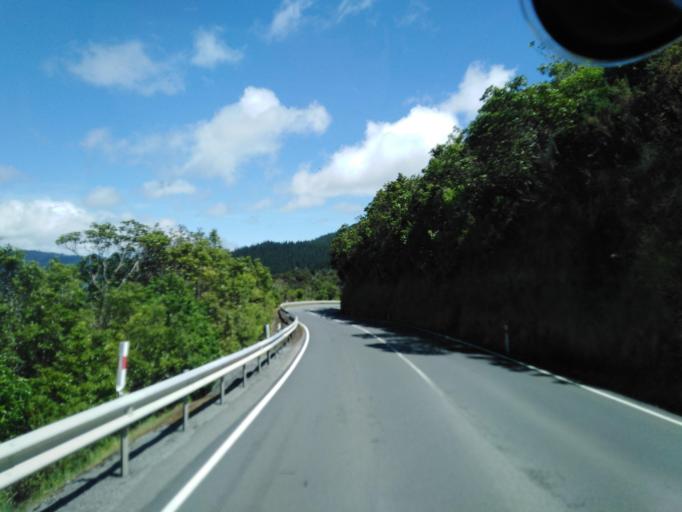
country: NZ
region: Nelson
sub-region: Nelson City
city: Nelson
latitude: -41.2290
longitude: 173.4338
